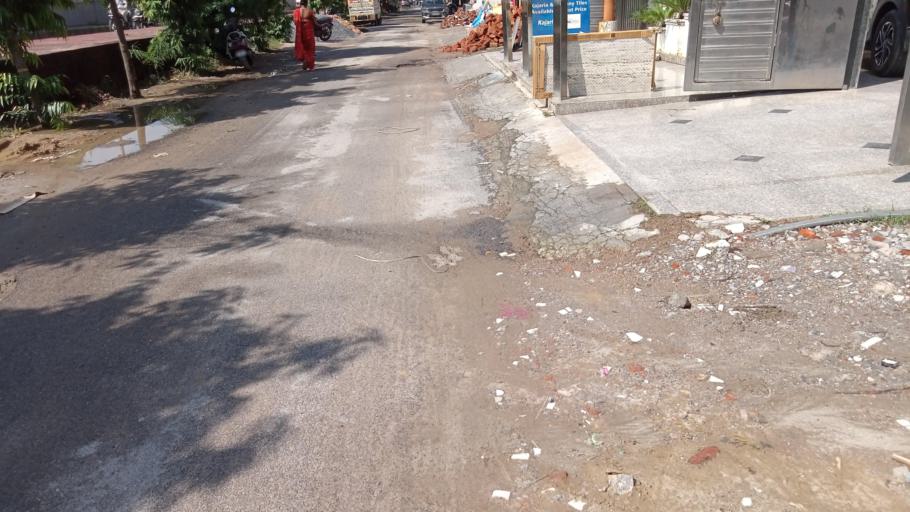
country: IN
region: Uttar Pradesh
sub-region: Ghaziabad
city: Ghaziabad
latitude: 28.6604
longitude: 77.3748
